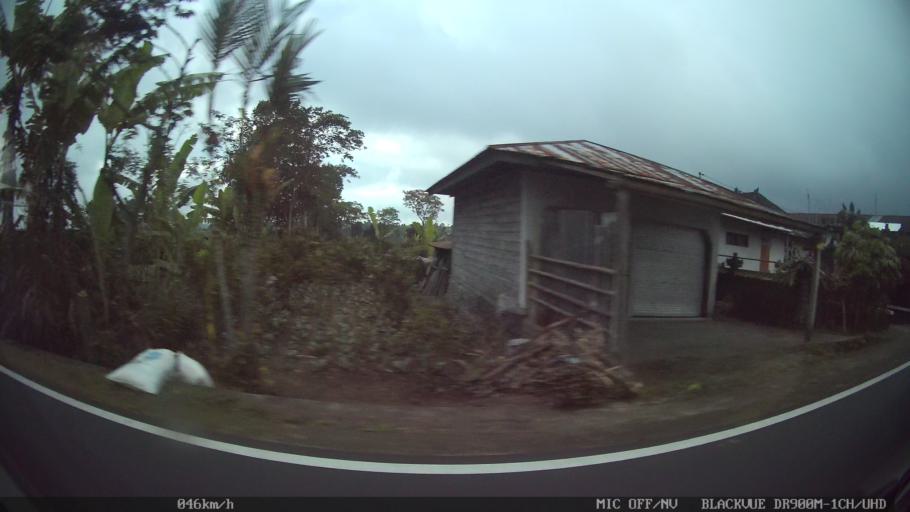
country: ID
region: Bali
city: Banjar Kedisan
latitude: -8.2746
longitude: 115.3291
